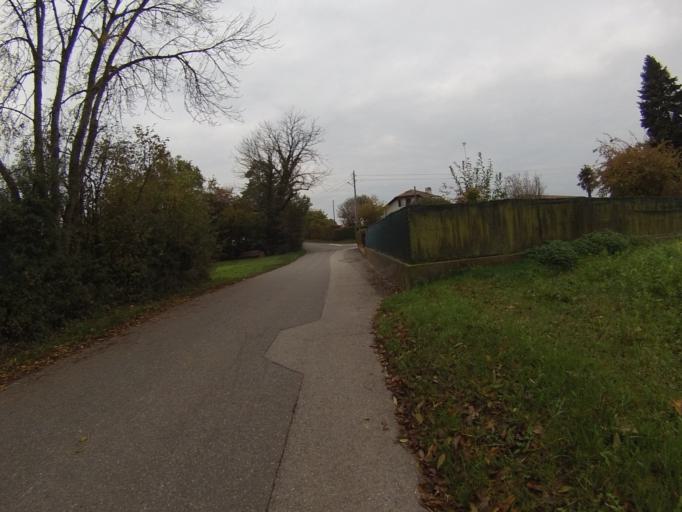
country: CH
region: Geneva
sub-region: Geneva
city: Meyrin
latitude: 46.2342
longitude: 6.0633
